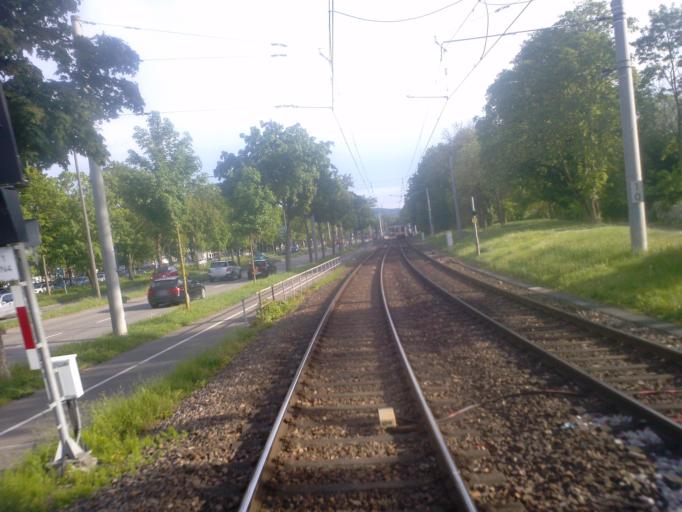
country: DE
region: Baden-Wuerttemberg
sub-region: Karlsruhe Region
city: Karlsruhe
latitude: 48.9869
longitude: 8.4034
